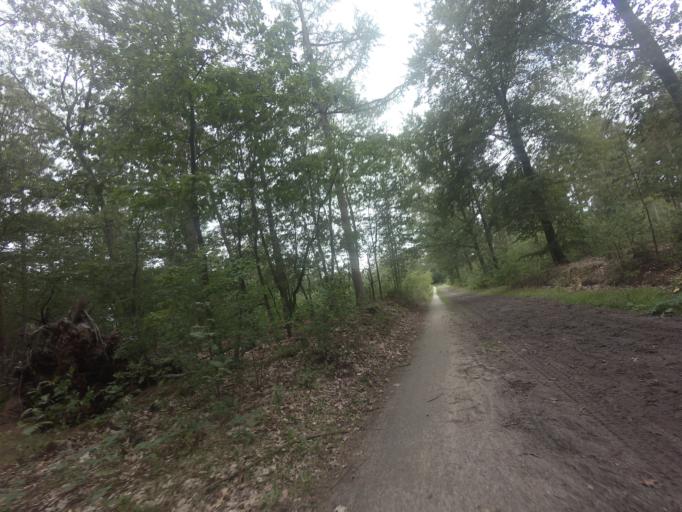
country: NL
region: Drenthe
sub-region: Gemeente Westerveld
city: Dwingeloo
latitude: 52.9232
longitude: 6.3259
